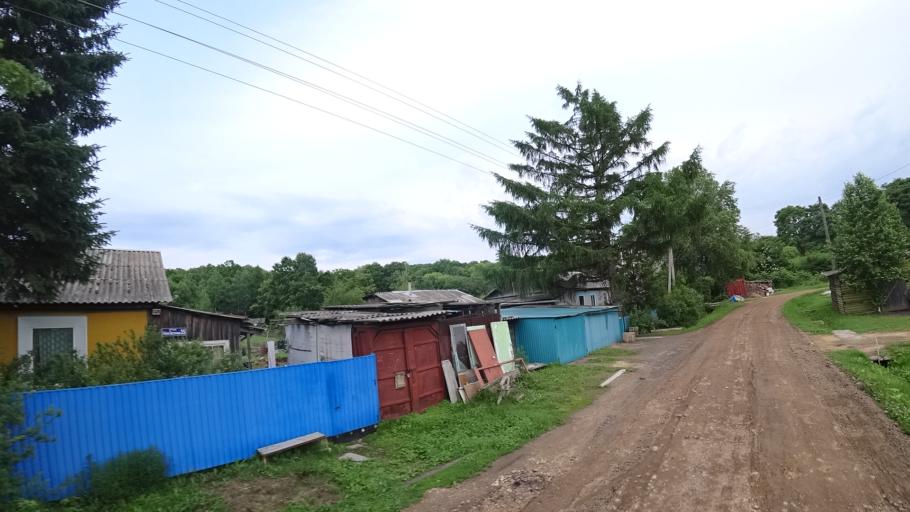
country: RU
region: Primorskiy
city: Novosysoyevka
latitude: 44.2348
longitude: 133.3803
